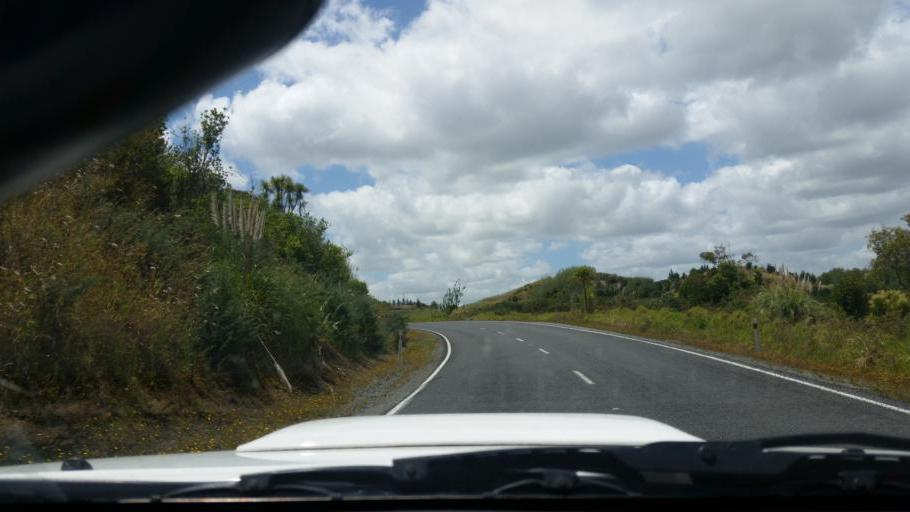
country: NZ
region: Northland
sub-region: Whangarei
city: Ruakaka
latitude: -36.0822
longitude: 174.2391
